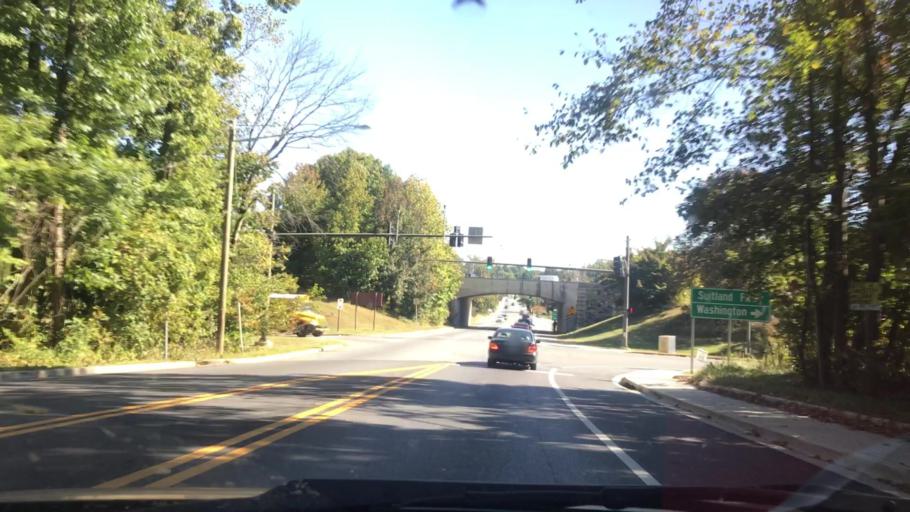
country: US
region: Maryland
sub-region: Prince George's County
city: Morningside
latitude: 38.8365
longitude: -76.9034
